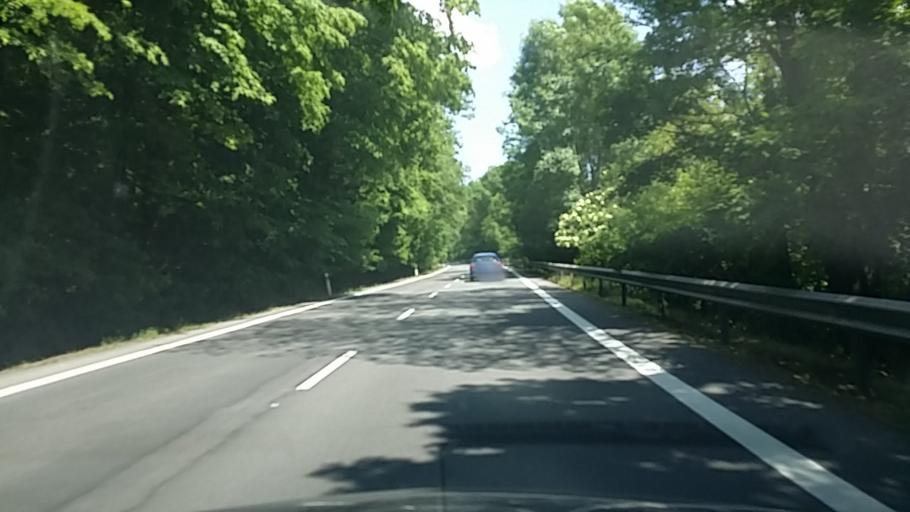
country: SK
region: Banskobystricky
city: Dudince
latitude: 48.2393
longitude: 18.9624
